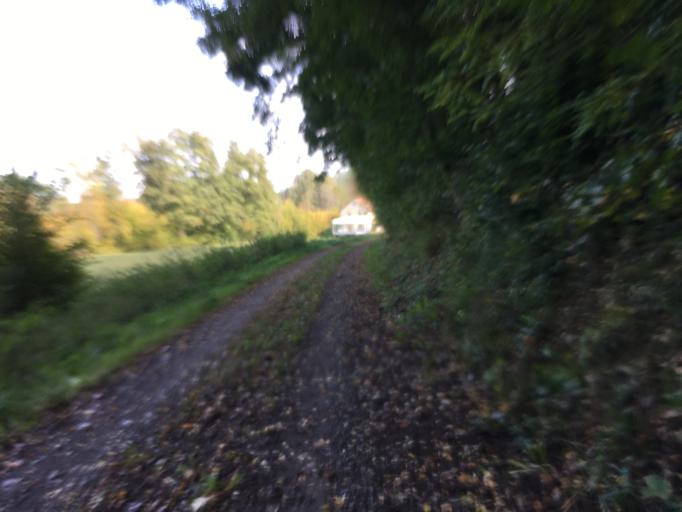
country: DE
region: Baden-Wuerttemberg
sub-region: Karlsruhe Region
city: Rosenberg
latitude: 49.3937
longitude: 9.5044
